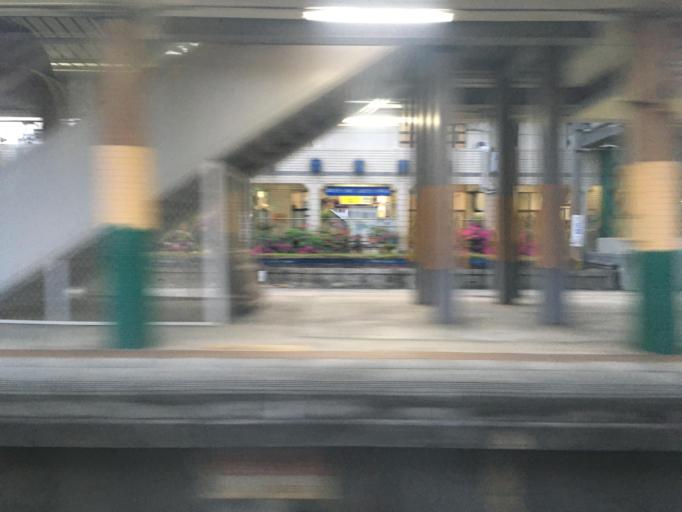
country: TW
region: Taiwan
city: Fengshan
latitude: 22.6563
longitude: 120.4213
